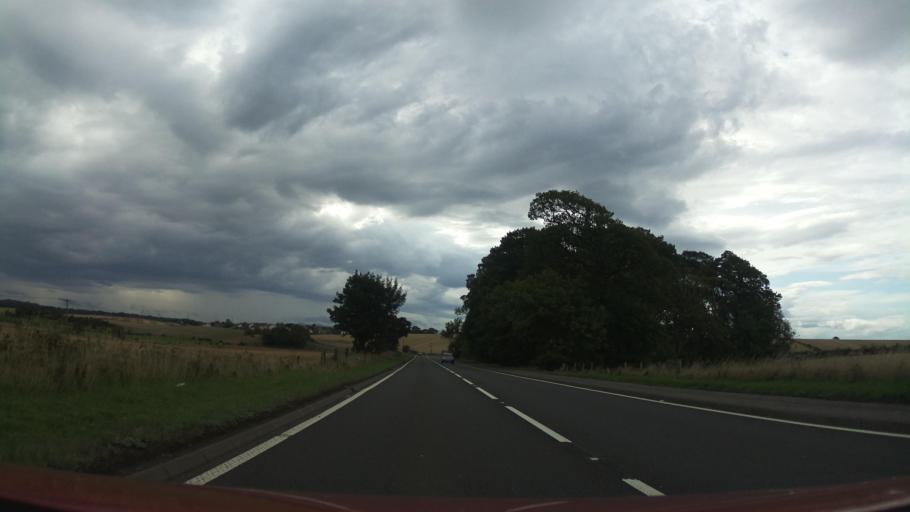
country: GB
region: Scotland
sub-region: Fife
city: Cairneyhill
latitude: 56.0548
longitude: -3.5408
